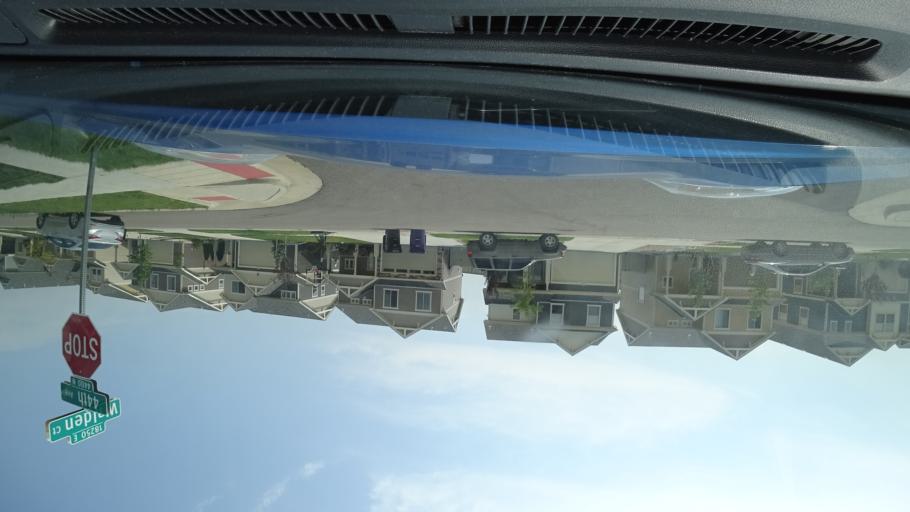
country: US
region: Colorado
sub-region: Adams County
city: Aurora
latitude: 39.7770
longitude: -104.7765
